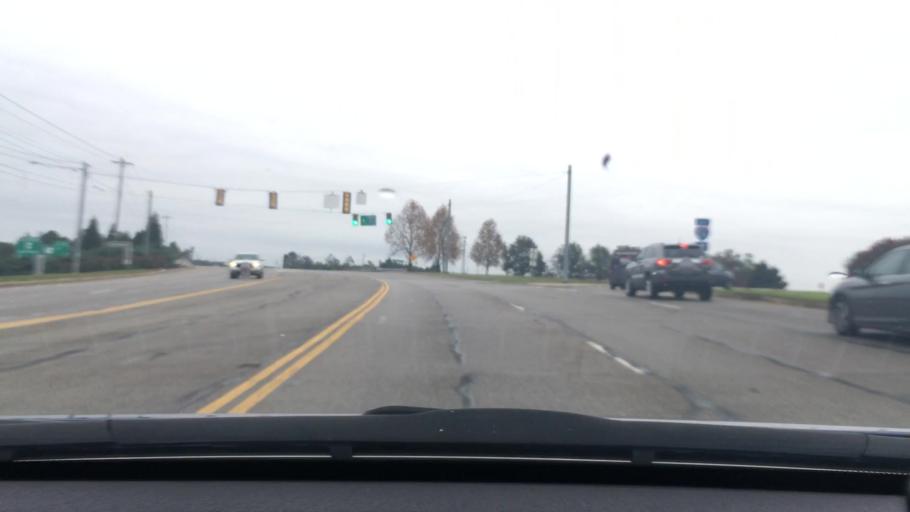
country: US
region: South Carolina
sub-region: Lexington County
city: Irmo
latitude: 34.0994
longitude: -81.1771
